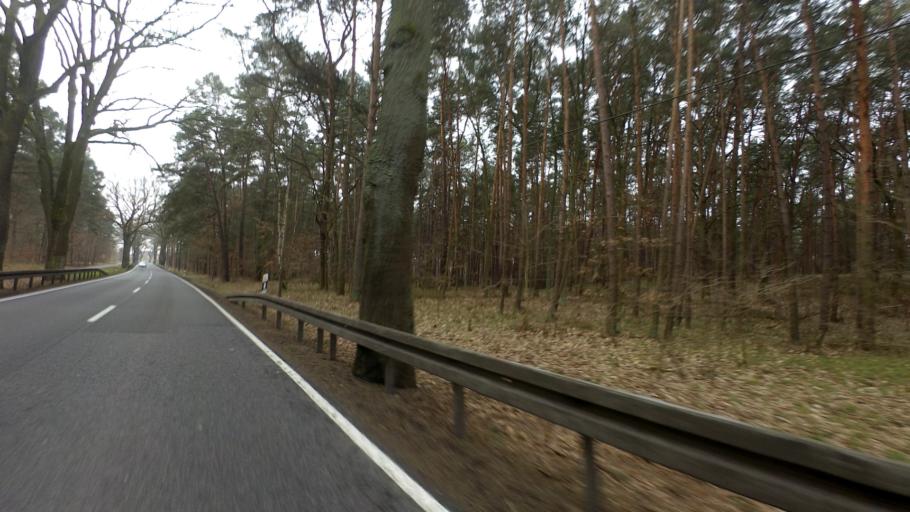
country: DE
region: Brandenburg
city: Beelitz
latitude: 52.2241
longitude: 12.9222
